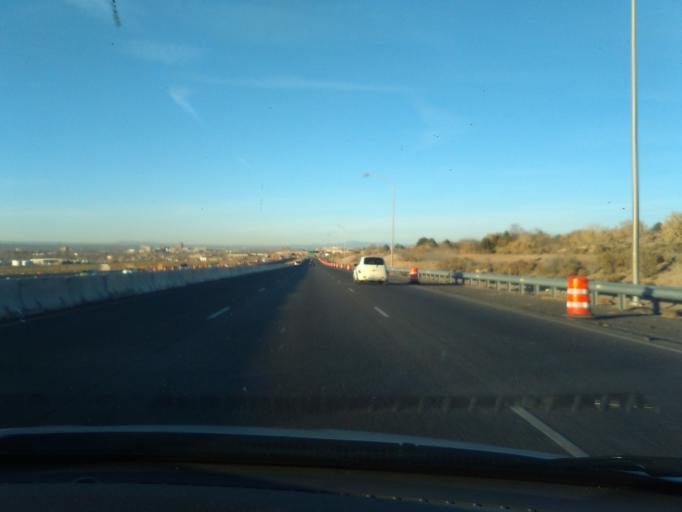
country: US
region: New Mexico
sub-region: Bernalillo County
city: South Valley
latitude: 35.0298
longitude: -106.6380
